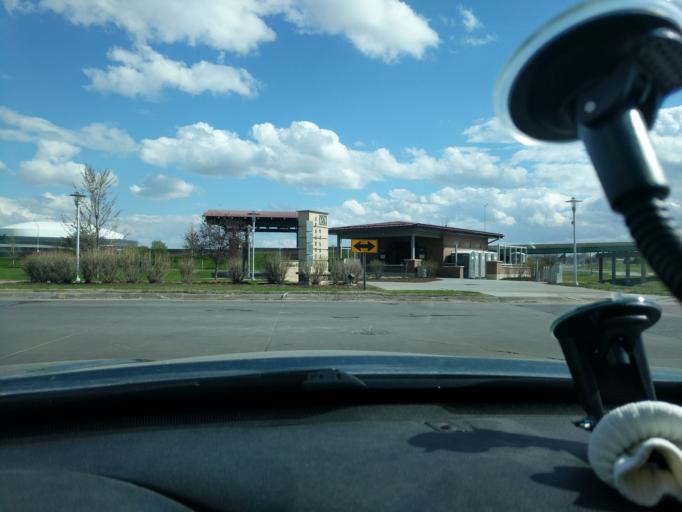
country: US
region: Nebraska
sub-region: Douglas County
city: Ralston
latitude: 41.2383
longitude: -96.0164
